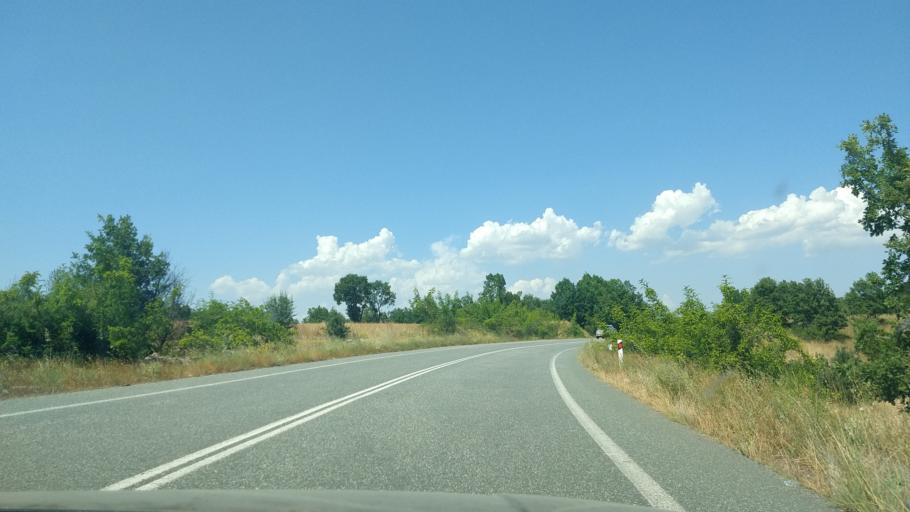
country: GR
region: West Macedonia
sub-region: Nomos Grevenon
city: Grevena
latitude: 40.0628
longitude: 21.4678
